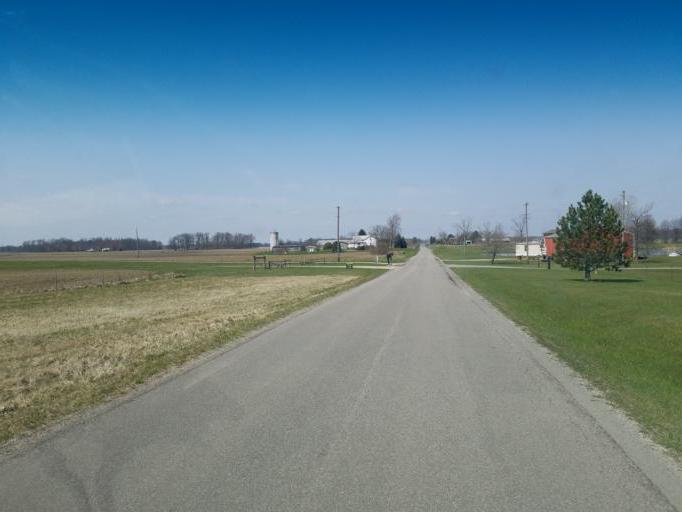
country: US
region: Ohio
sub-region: Wyandot County
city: Upper Sandusky
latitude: 40.8762
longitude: -83.3320
